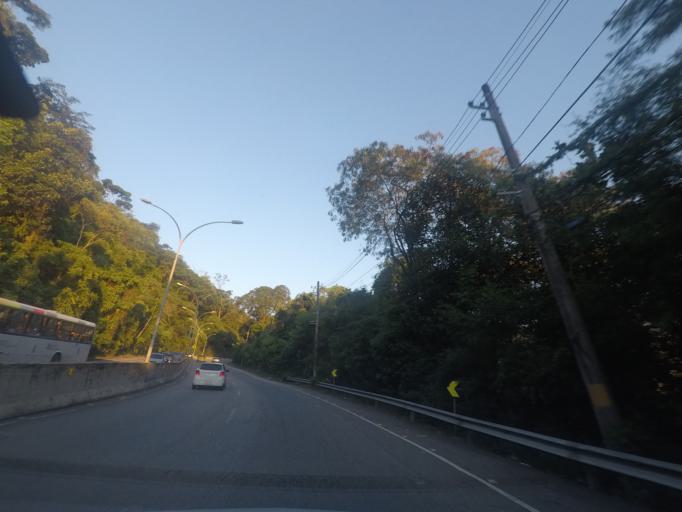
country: BR
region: Rio de Janeiro
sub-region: Rio De Janeiro
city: Rio de Janeiro
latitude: -22.9230
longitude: -43.3037
